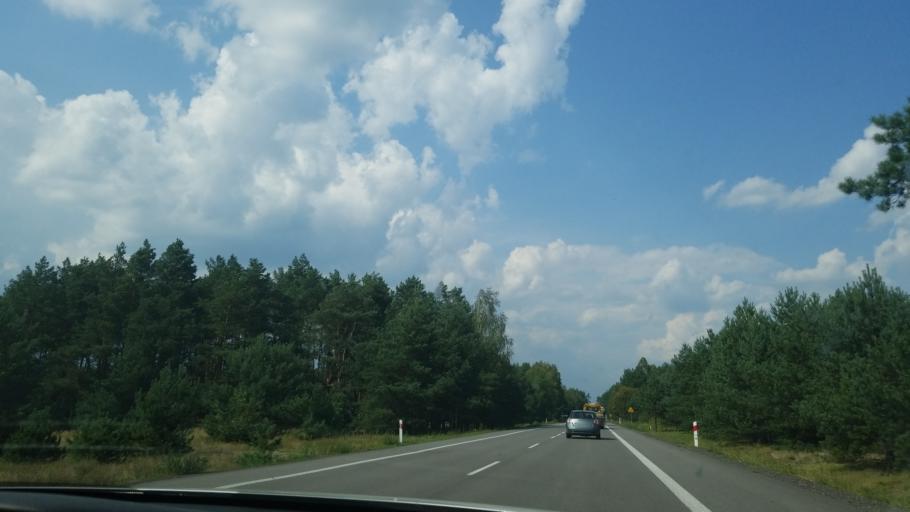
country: PL
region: Subcarpathian Voivodeship
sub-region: Powiat nizanski
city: Jarocin
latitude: 50.6272
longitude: 22.2866
